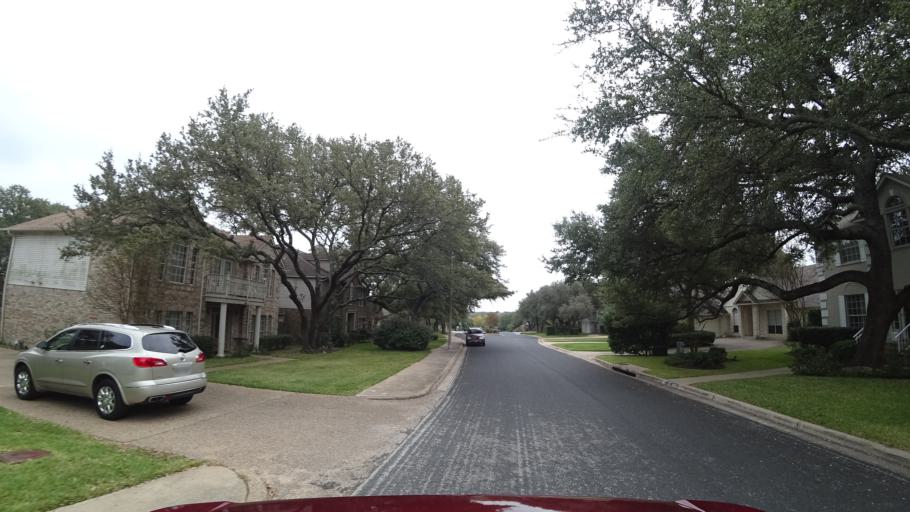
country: US
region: Texas
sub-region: Williamson County
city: Anderson Mill
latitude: 30.4417
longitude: -97.8256
